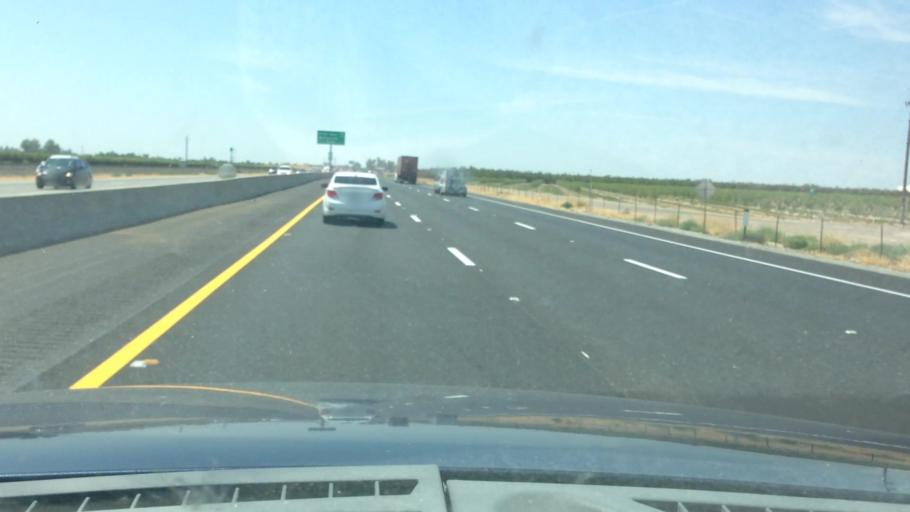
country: US
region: California
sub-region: Kern County
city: McFarland
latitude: 35.7039
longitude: -119.2332
